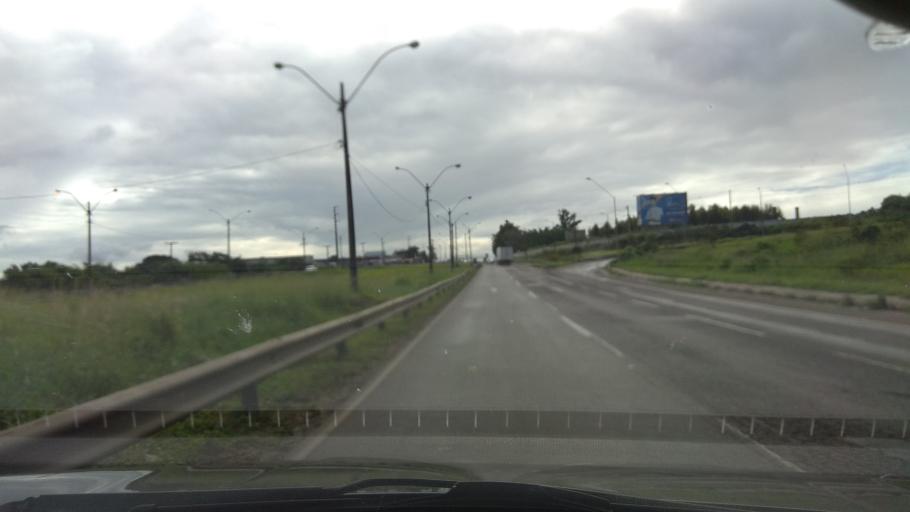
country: BR
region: Bahia
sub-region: Feira De Santana
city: Feira de Santana
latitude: -12.2999
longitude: -38.8987
